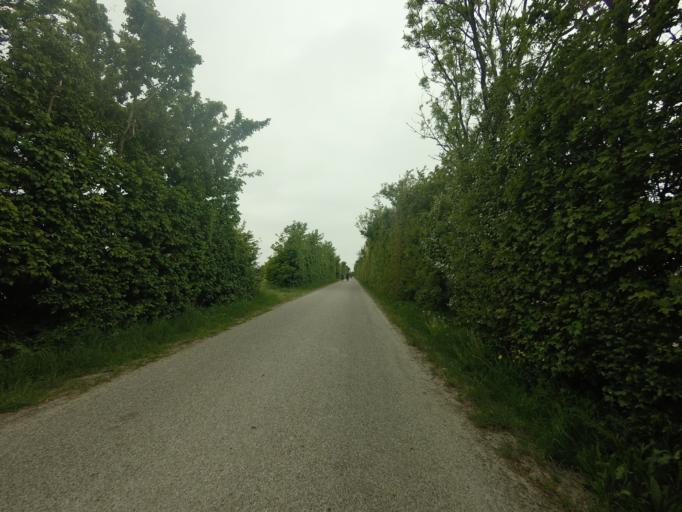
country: NL
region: Zeeland
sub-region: Gemeente Middelburg
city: Middelburg
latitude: 51.5516
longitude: 3.5737
